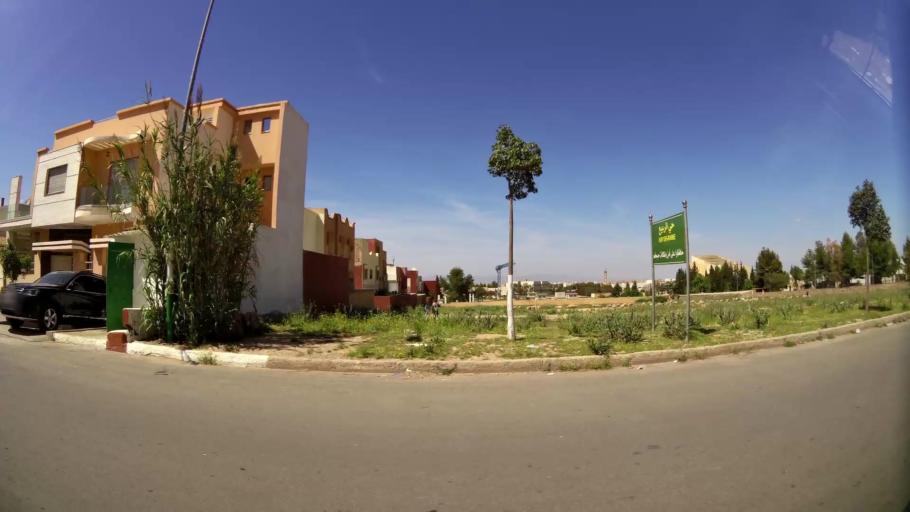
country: MA
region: Oriental
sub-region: Oujda-Angad
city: Oujda
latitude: 34.6483
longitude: -1.9032
